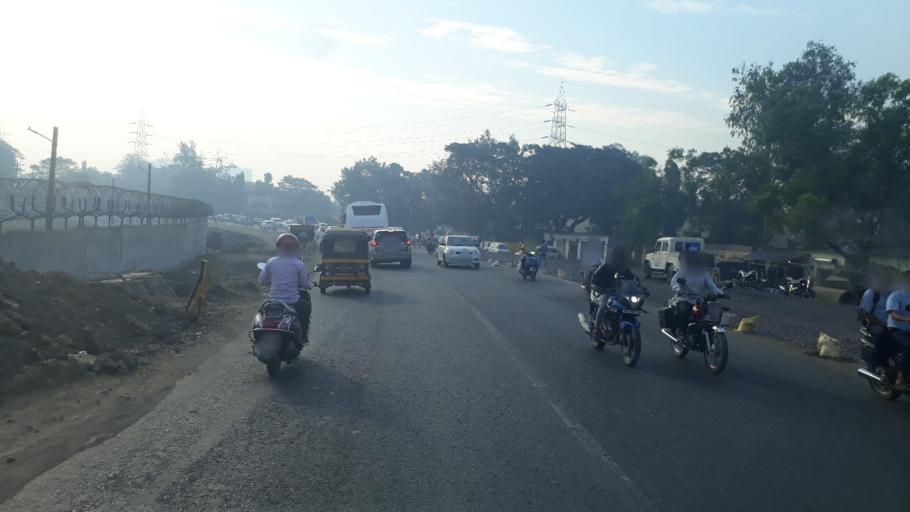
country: IN
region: Maharashtra
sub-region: Raigarh
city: Kalundri
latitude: 18.9764
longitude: 73.1172
